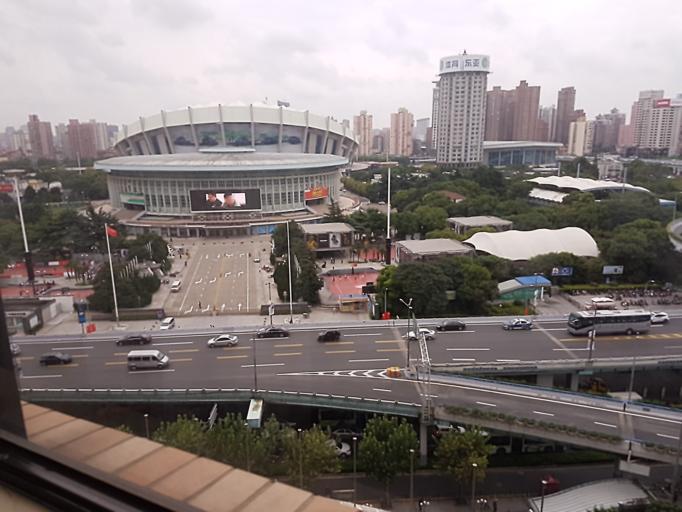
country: CN
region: Shanghai Shi
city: Xuhui
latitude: 31.1835
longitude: 121.4306
